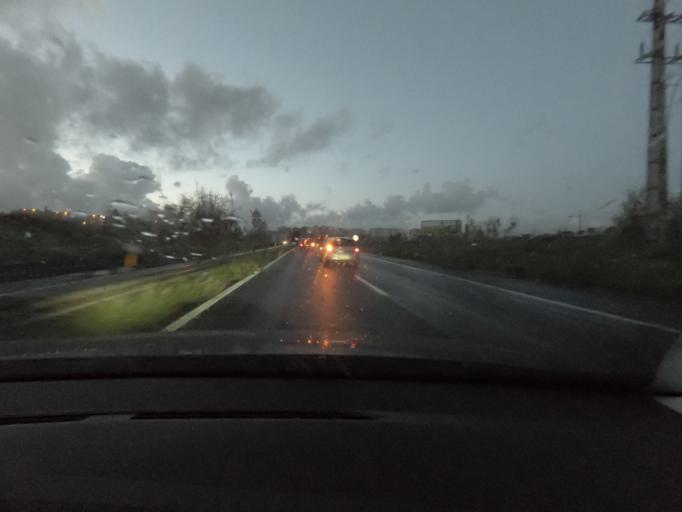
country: PT
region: Lisbon
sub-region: Oeiras
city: Barcarena
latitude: 38.7373
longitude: -9.2987
